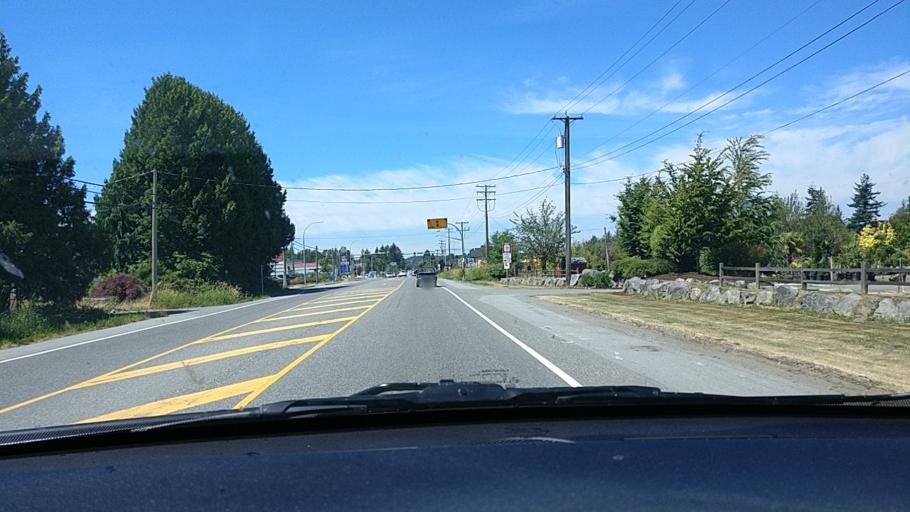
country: CA
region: British Columbia
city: Aldergrove
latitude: 49.0573
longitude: -122.4459
